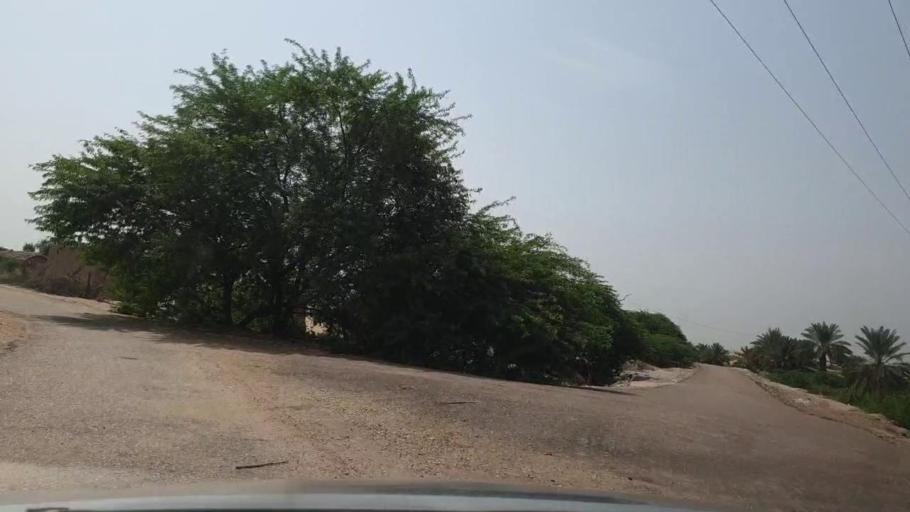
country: PK
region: Sindh
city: Pano Aqil
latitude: 27.6110
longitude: 69.1458
